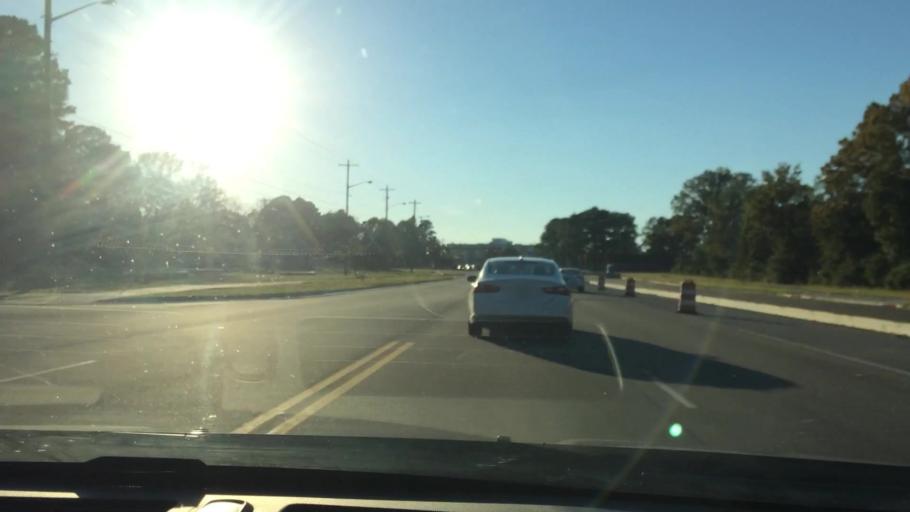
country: US
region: North Carolina
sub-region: Pitt County
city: Greenville
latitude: 35.6081
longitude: -77.3881
